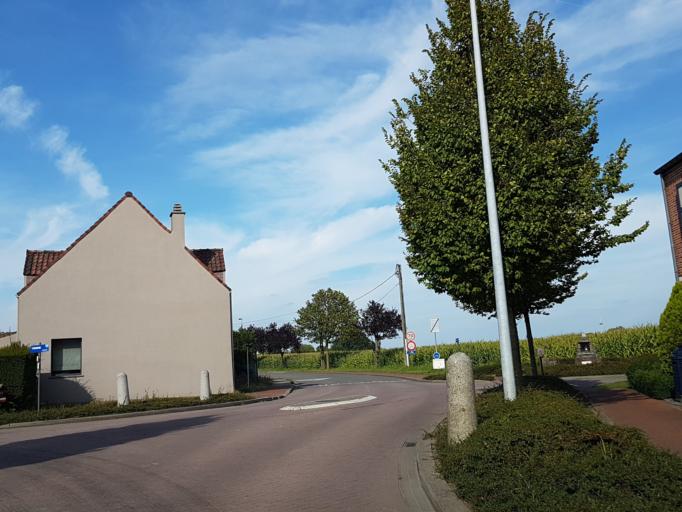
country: BE
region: Flanders
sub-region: Provincie Vlaams-Brabant
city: Zemst
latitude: 50.9951
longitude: 4.4209
